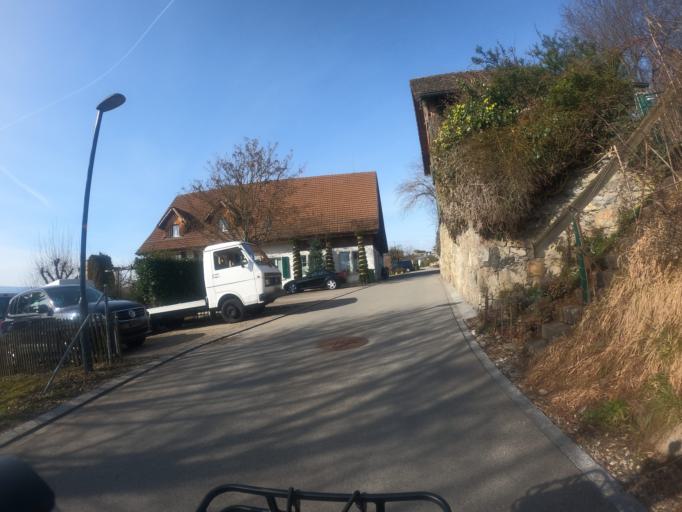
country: CH
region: Zurich
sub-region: Bezirk Affoltern
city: Mettmenstetten
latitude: 47.2468
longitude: 8.4666
